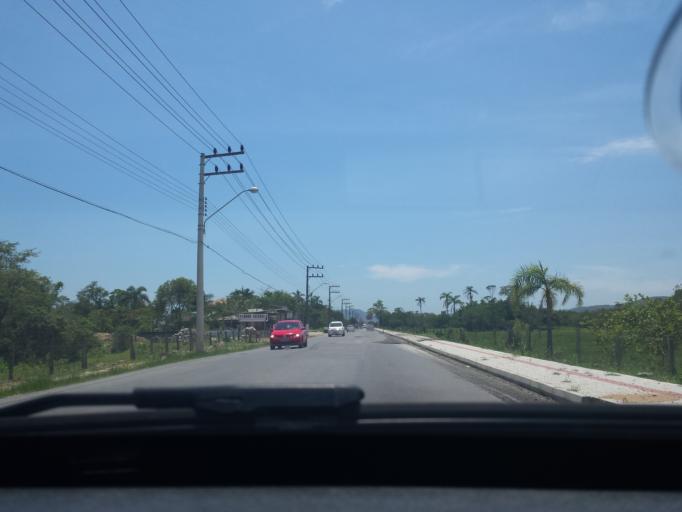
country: BR
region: Santa Catarina
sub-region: Porto Belo
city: Porto Belo
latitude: -27.1614
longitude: -48.6060
